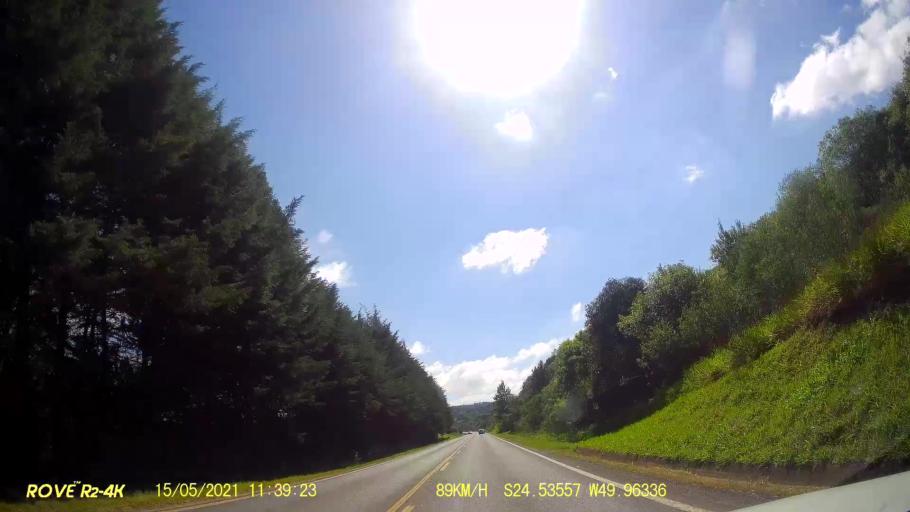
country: BR
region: Parana
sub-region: Pirai Do Sul
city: Pirai do Sul
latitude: -24.5352
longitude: -49.9633
